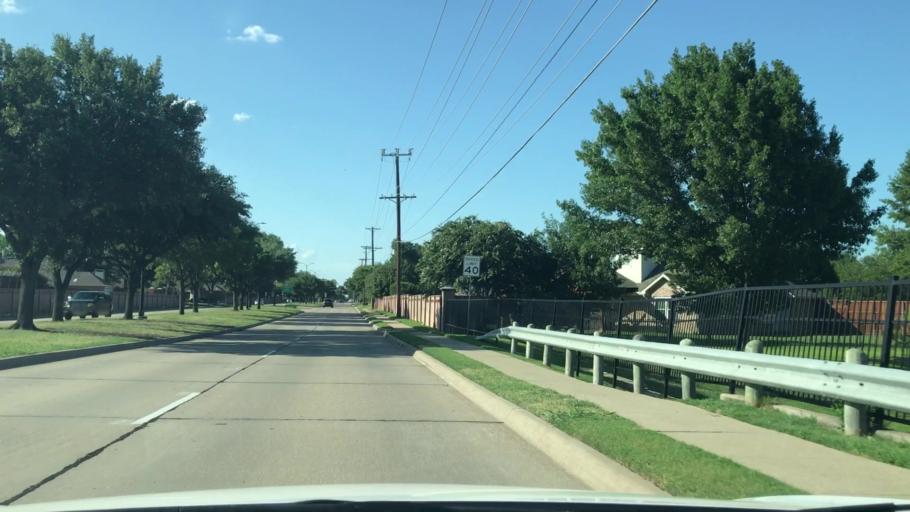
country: US
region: Texas
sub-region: Collin County
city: Frisco
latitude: 33.1127
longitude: -96.7880
